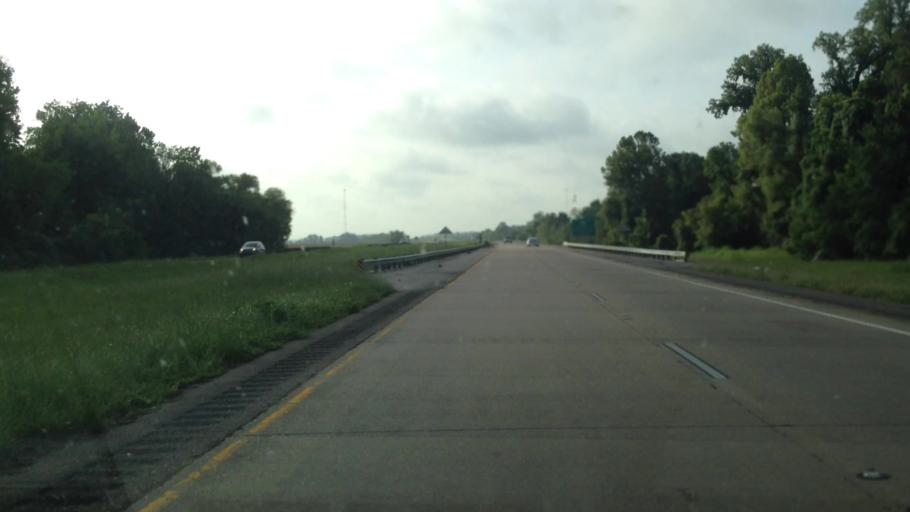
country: US
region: Louisiana
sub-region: Rapides Parish
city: Lecompte
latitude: 31.0207
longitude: -92.3906
